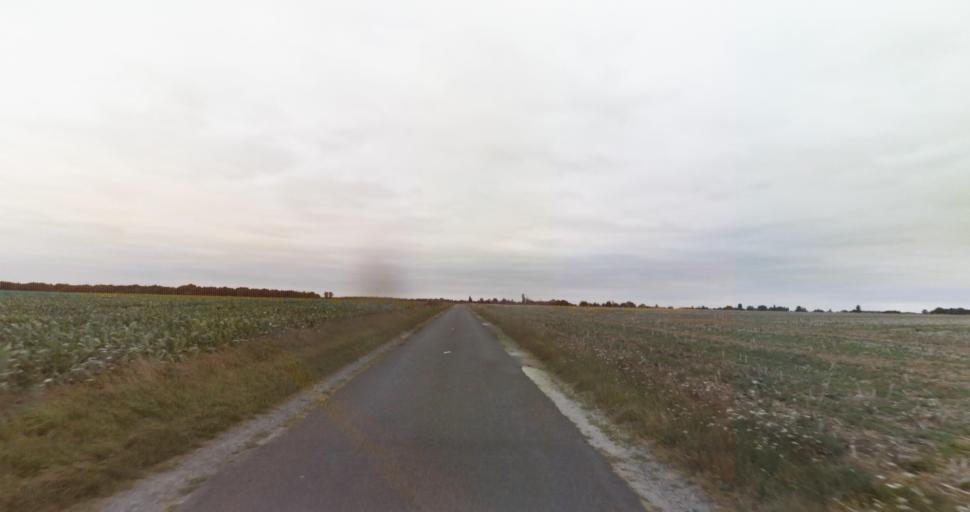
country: FR
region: Haute-Normandie
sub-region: Departement de l'Eure
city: Marcilly-sur-Eure
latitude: 48.8250
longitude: 1.2943
